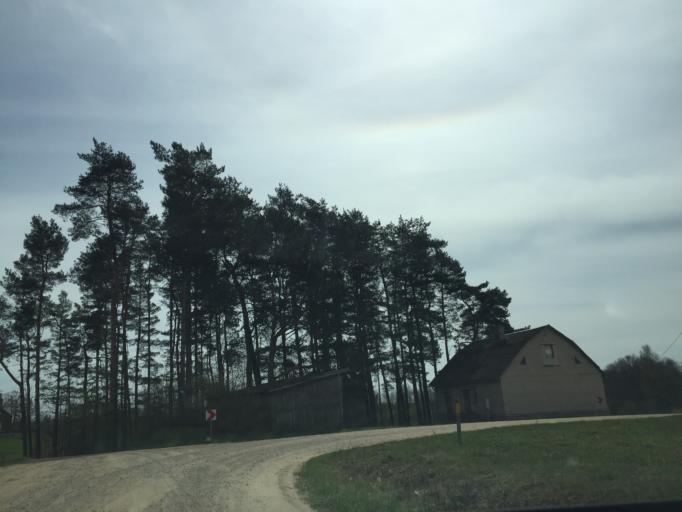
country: LV
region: Ludzas Rajons
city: Ludza
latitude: 56.5647
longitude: 27.5599
